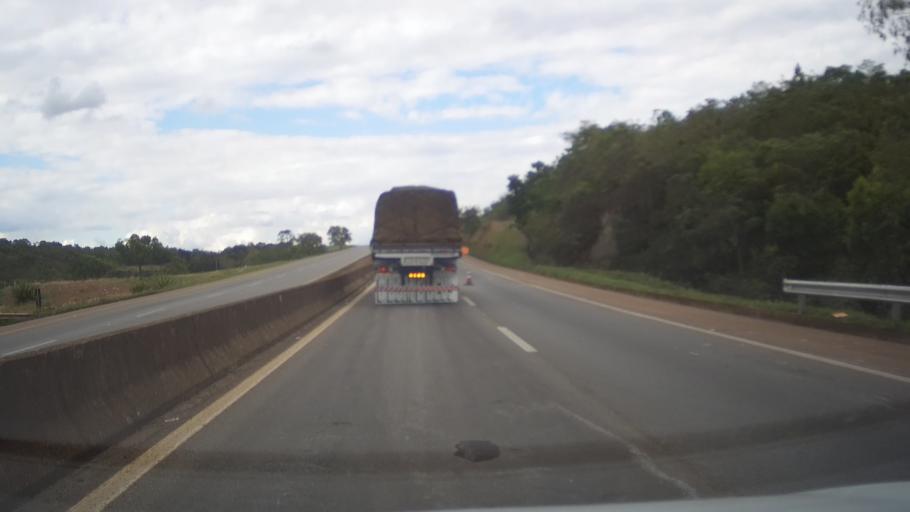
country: BR
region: Minas Gerais
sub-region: Itauna
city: Itauna
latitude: -20.3108
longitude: -44.4501
